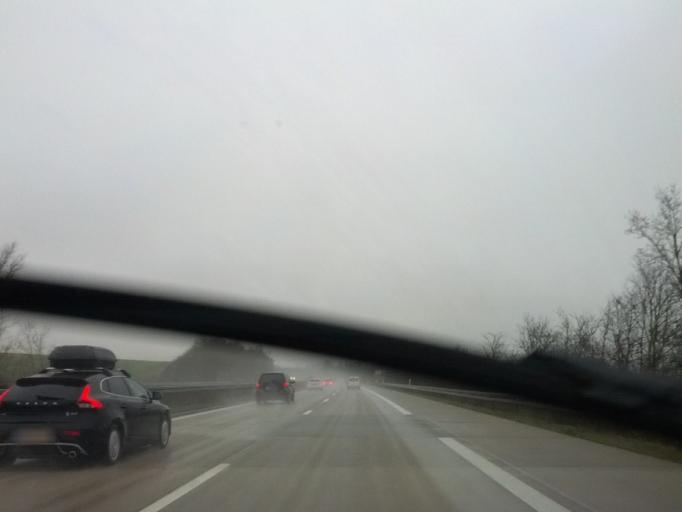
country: DE
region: Bavaria
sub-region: Regierungsbezirk Mittelfranken
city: Schopfloch
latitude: 49.1437
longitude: 10.2641
